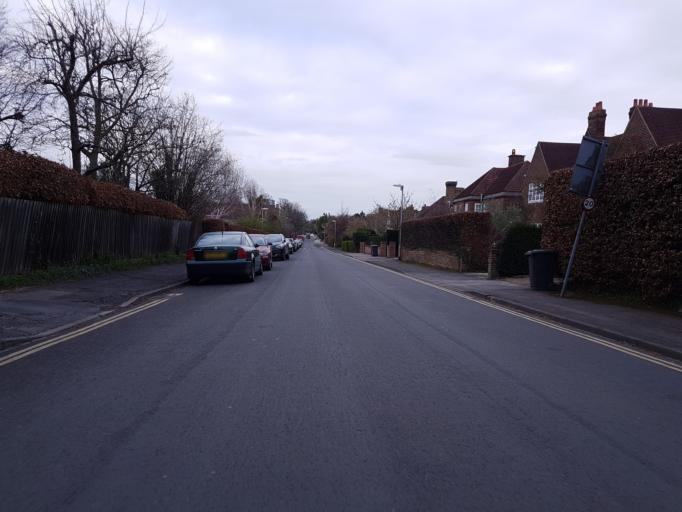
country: GB
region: England
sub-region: Cambridgeshire
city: Cambridge
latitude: 52.2154
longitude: 0.1005
